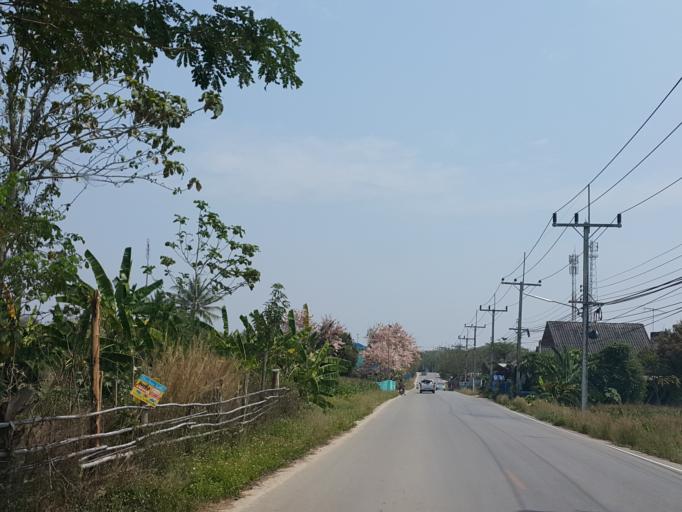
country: TH
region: Lampang
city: Chae Hom
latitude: 18.7579
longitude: 99.5654
